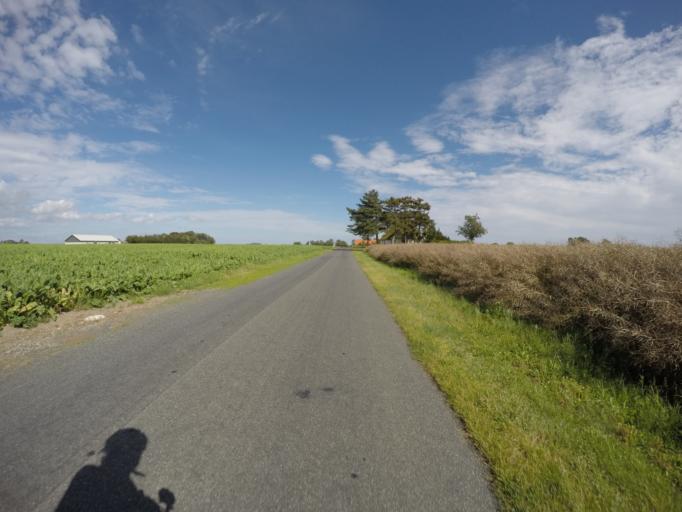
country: SE
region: Skane
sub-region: Simrishamns Kommun
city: Simrishamn
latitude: 55.4878
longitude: 14.1870
